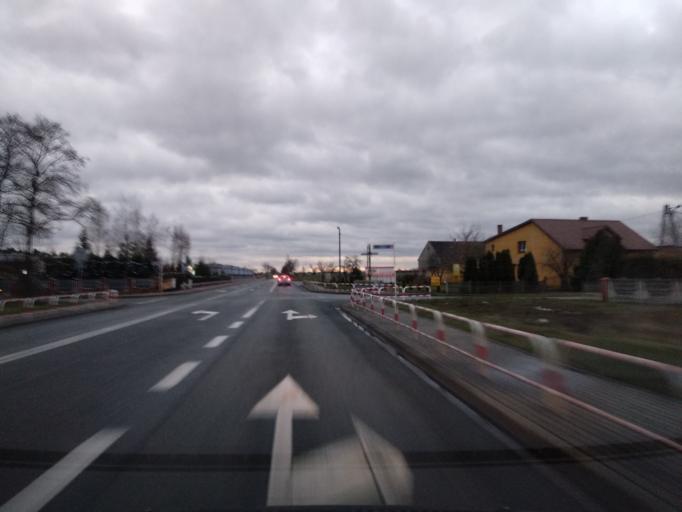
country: PL
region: Greater Poland Voivodeship
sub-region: Powiat koninski
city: Rychwal
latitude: 52.0957
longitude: 18.1665
